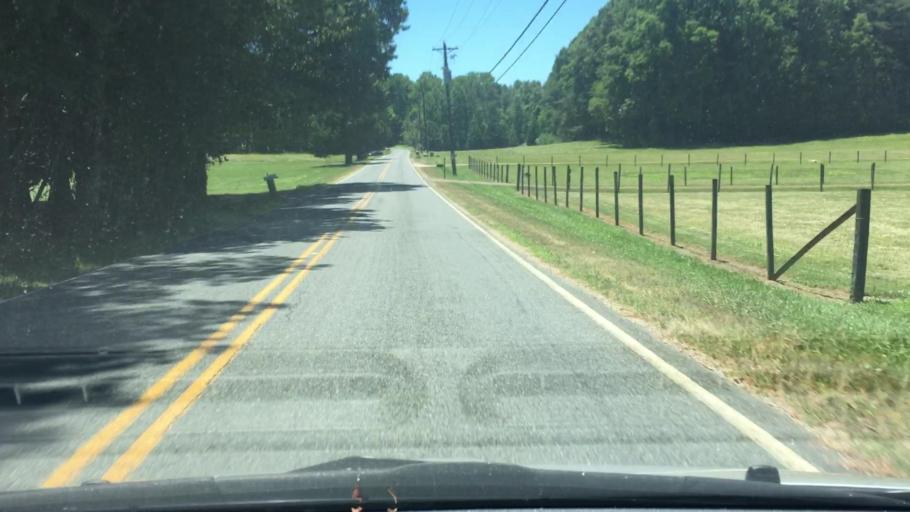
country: US
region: Maryland
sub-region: Saint Mary's County
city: California
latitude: 38.3815
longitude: -76.5770
